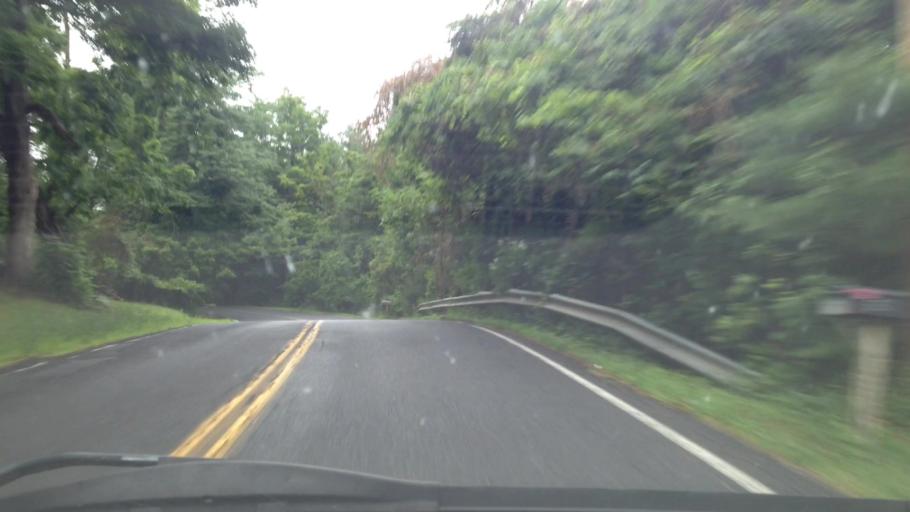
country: US
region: New York
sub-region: Ulster County
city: New Paltz
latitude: 41.7790
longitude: -74.0664
